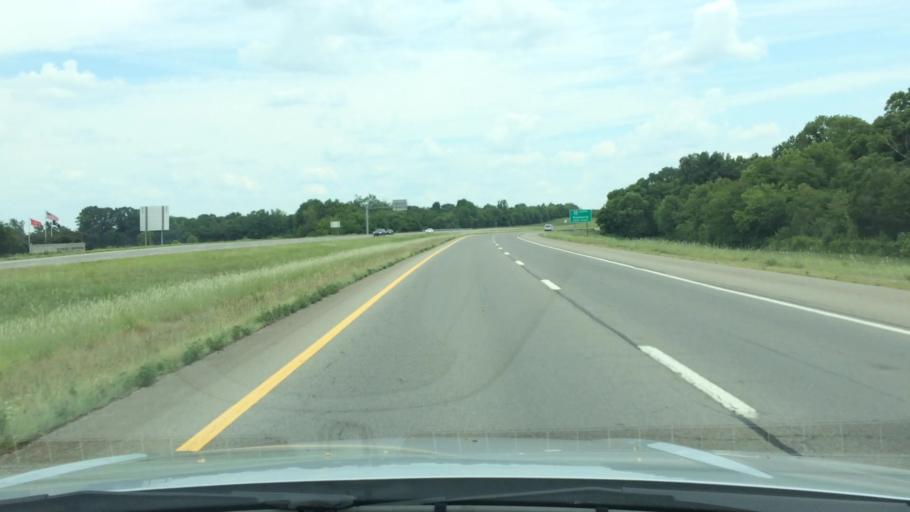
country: US
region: Tennessee
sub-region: Maury County
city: Spring Hill
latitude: 35.7375
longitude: -86.8840
